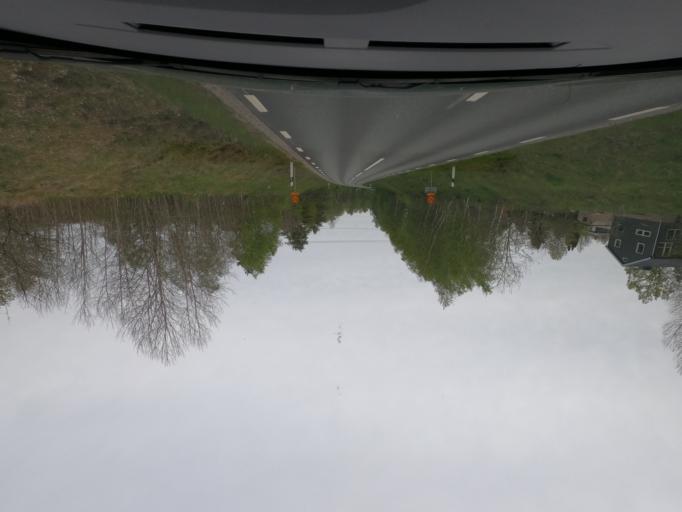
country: SE
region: Joenkoeping
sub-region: Varnamo Kommun
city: Bredaryd
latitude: 57.2161
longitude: 13.7750
